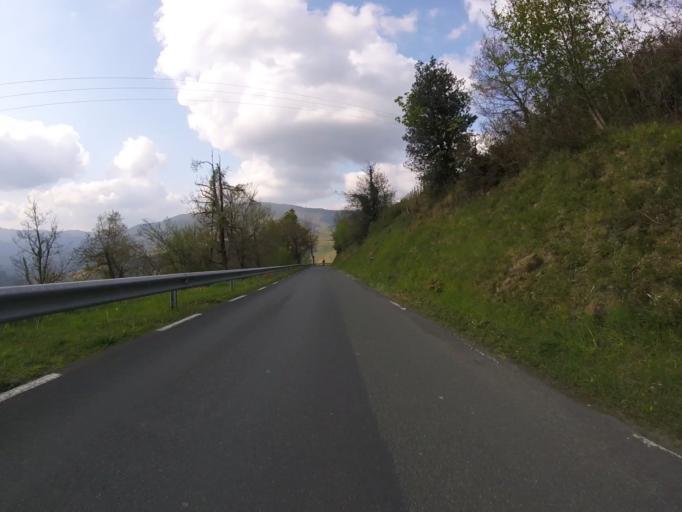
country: ES
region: Basque Country
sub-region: Provincia de Guipuzcoa
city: Azkoitia
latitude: 43.2058
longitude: -2.3532
